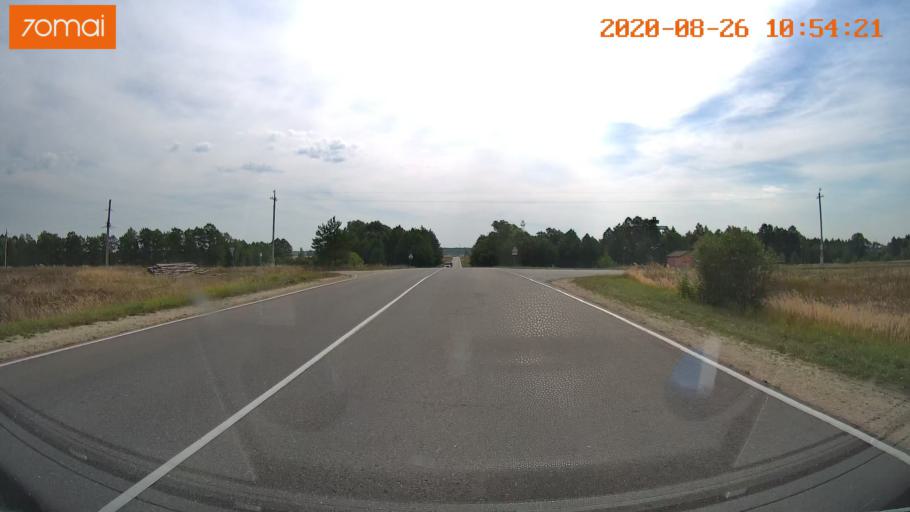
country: RU
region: Rjazan
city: Izhevskoye
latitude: 54.6295
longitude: 41.1604
